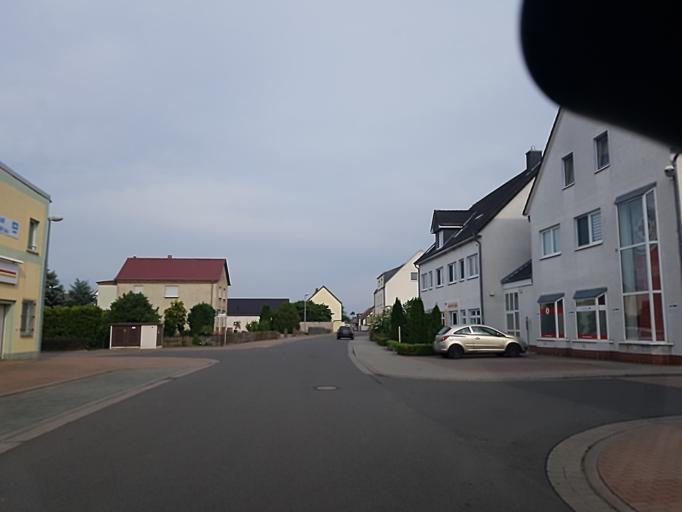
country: DE
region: Saxony-Anhalt
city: Elster
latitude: 51.8285
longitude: 12.8266
